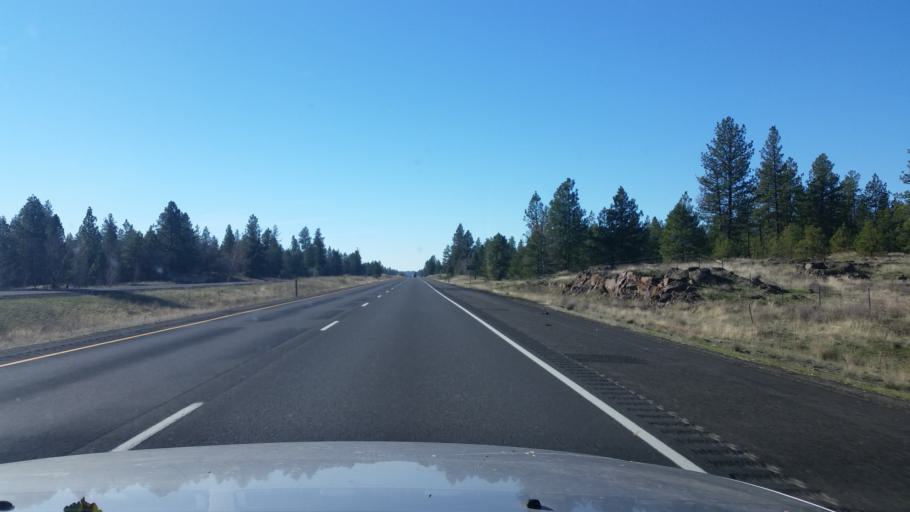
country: US
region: Washington
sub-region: Spokane County
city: Medical Lake
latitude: 47.4683
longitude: -117.7440
